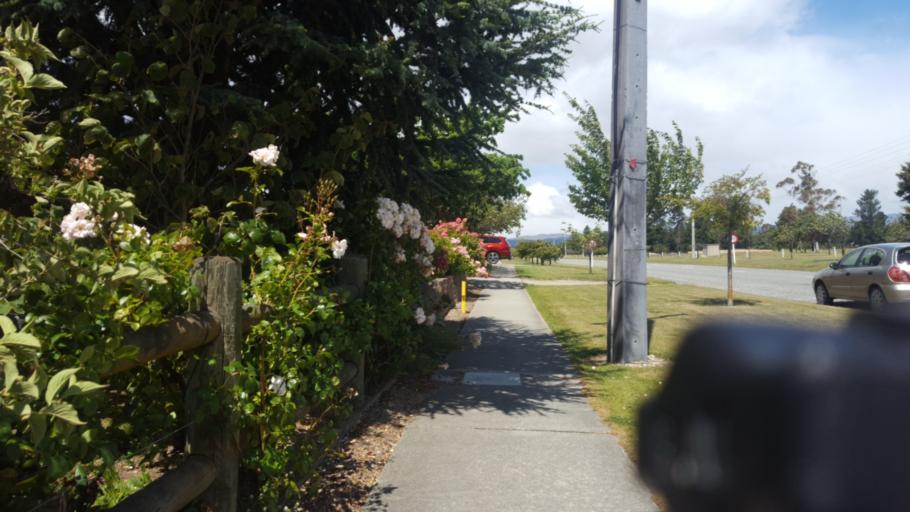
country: NZ
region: Otago
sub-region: Queenstown-Lakes District
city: Wanaka
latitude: -45.1942
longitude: 169.3263
